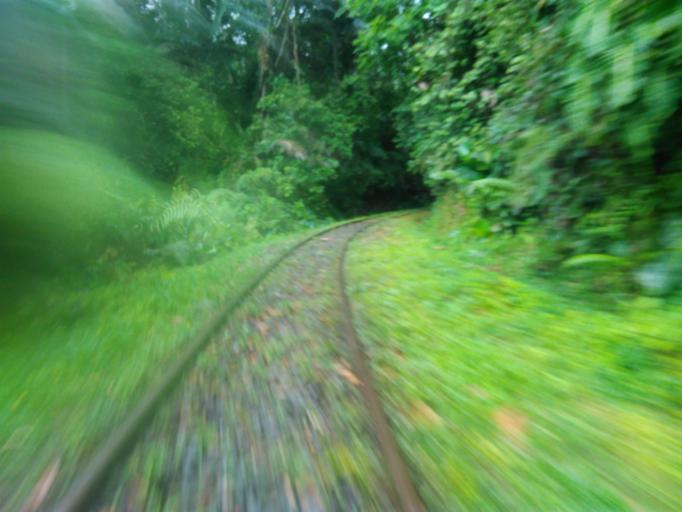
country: CO
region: Valle del Cauca
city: Buenaventura
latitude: 3.8489
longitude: -76.8848
